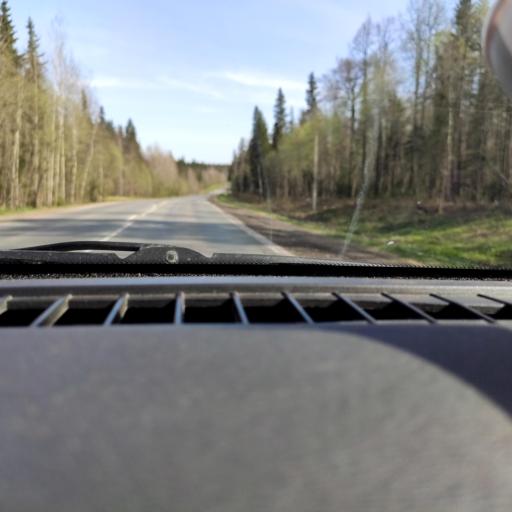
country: RU
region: Perm
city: Perm
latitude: 58.2065
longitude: 56.1968
